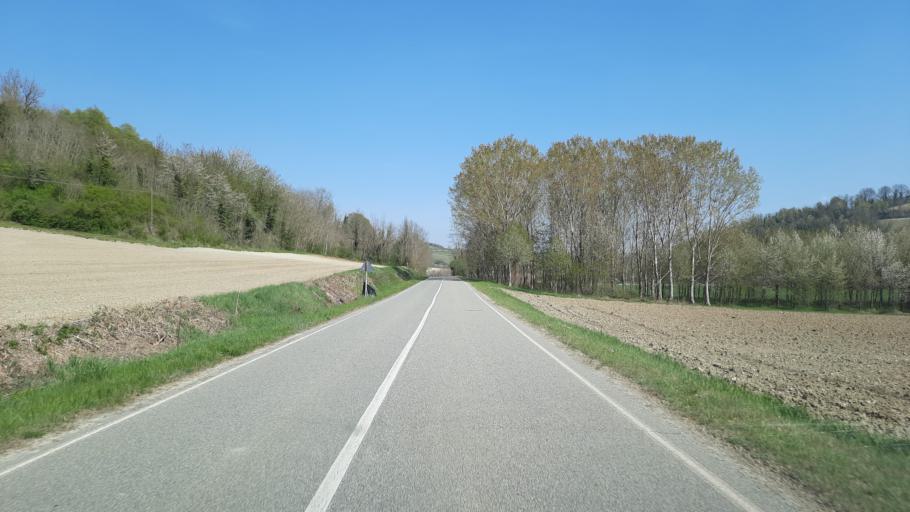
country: IT
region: Piedmont
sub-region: Provincia di Alessandria
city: Olivola
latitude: 45.0297
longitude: 8.3684
